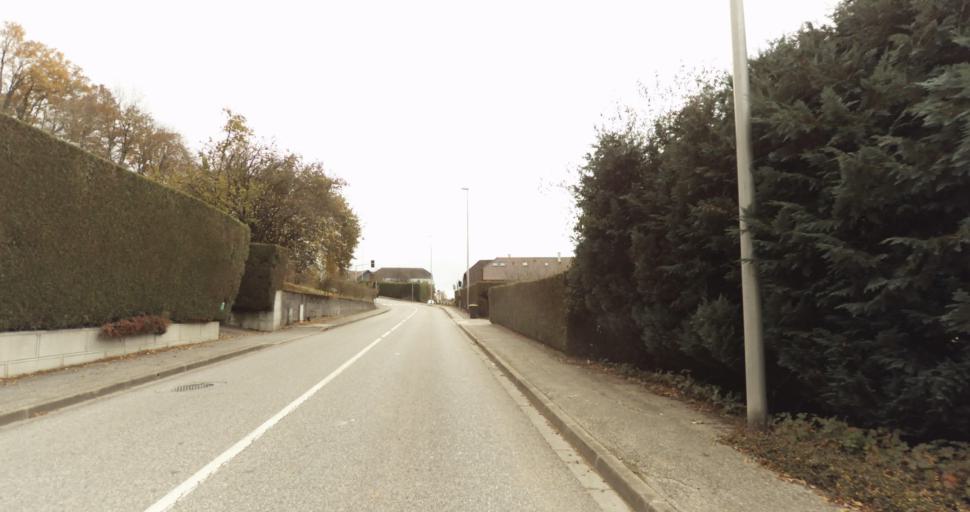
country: FR
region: Rhone-Alpes
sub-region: Departement de la Haute-Savoie
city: Annecy-le-Vieux
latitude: 45.9297
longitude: 6.1400
